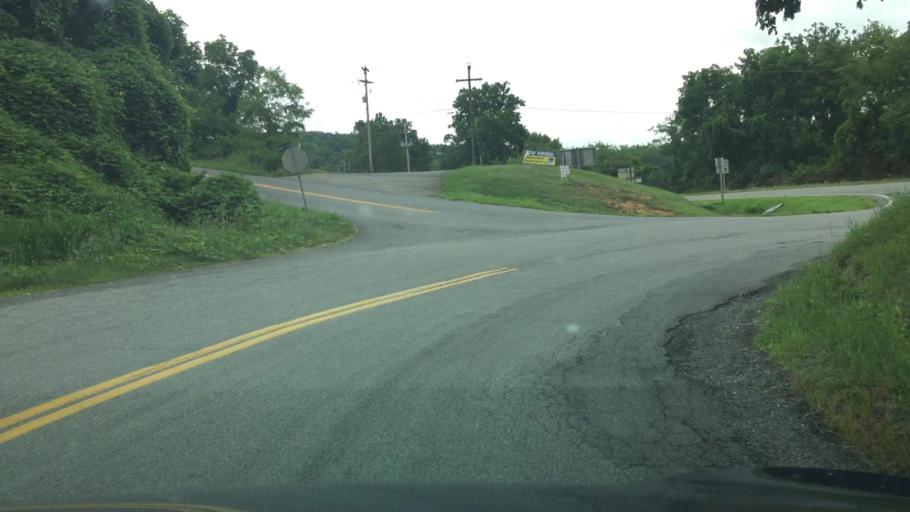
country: US
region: Virginia
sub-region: Pulaski County
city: Pulaski
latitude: 36.9908
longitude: -80.7908
